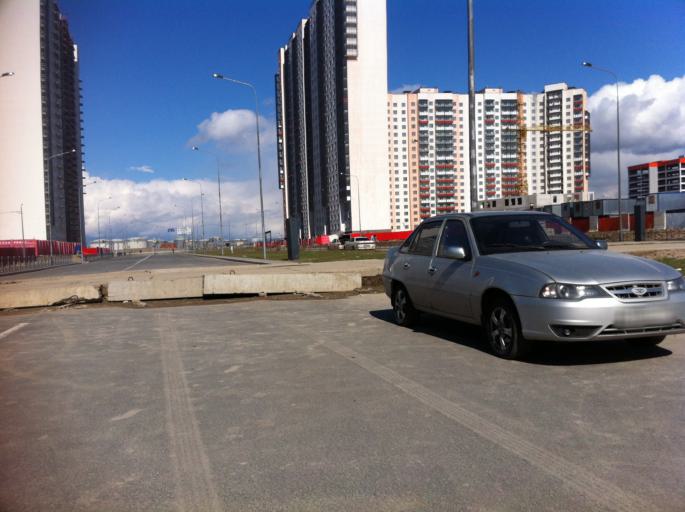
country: RU
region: St.-Petersburg
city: Uritsk
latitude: 59.8681
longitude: 30.1580
